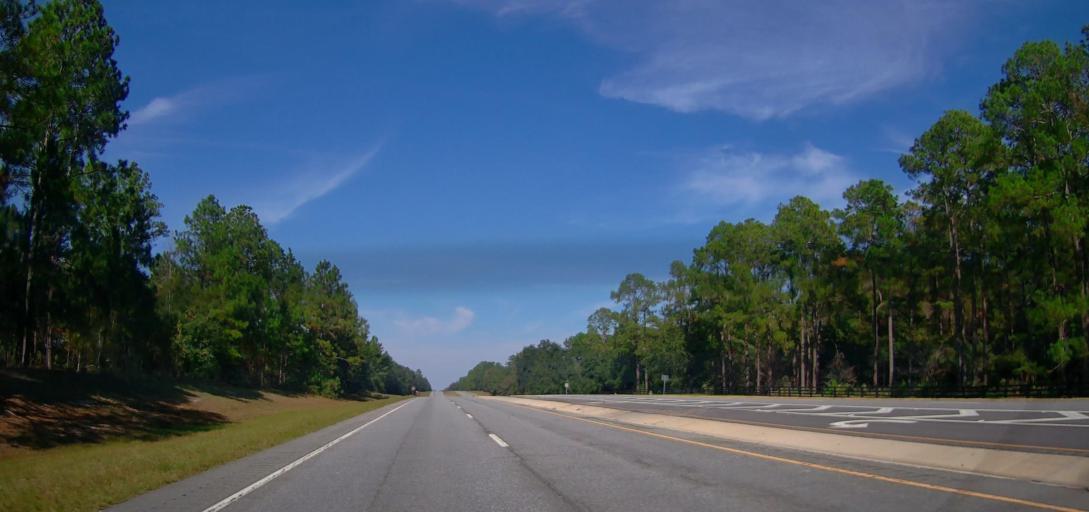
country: US
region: Georgia
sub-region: Lee County
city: Leesburg
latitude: 31.6824
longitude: -83.9944
